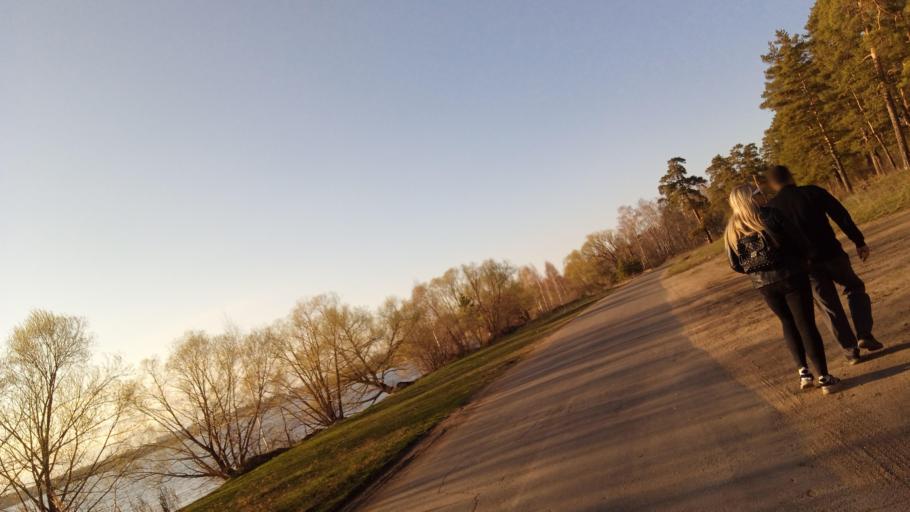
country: RU
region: Chelyabinsk
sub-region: Gorod Chelyabinsk
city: Chelyabinsk
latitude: 55.1309
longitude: 61.3282
